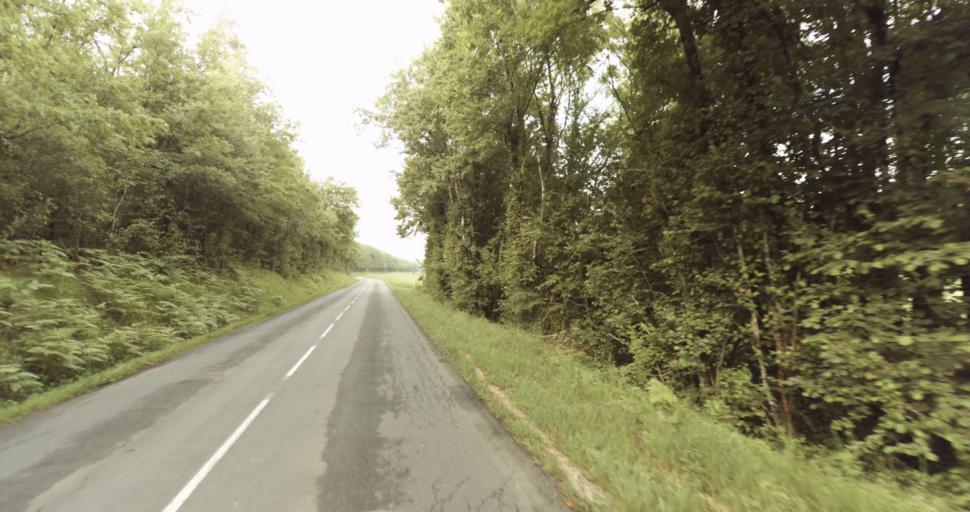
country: FR
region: Aquitaine
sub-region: Departement de la Dordogne
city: Lalinde
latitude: 44.9171
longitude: 0.6790
